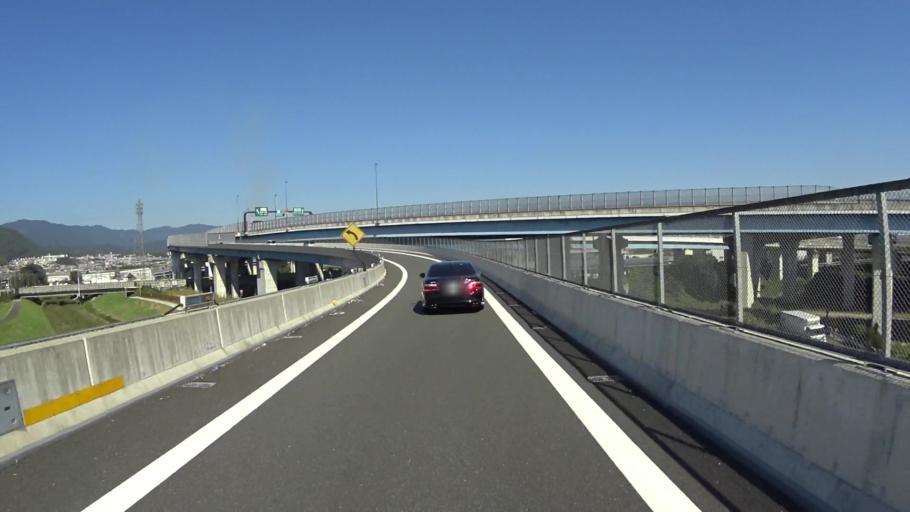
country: JP
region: Kyoto
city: Yawata
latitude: 34.9010
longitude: 135.6964
